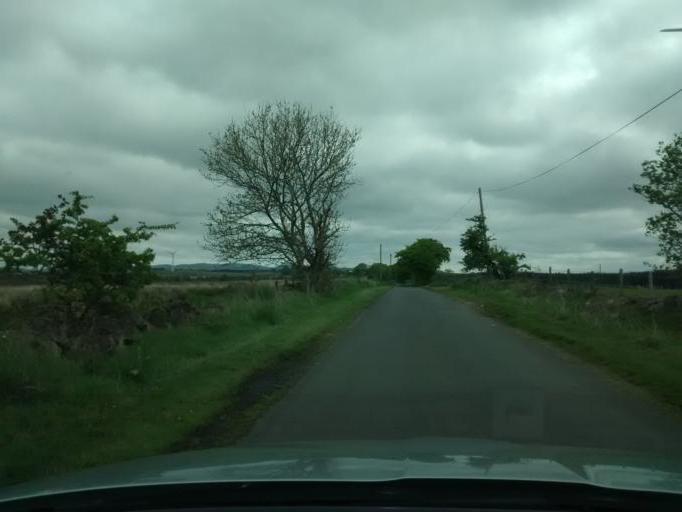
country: GB
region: Scotland
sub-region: North Lanarkshire
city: Harthill
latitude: 55.8789
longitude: -3.7490
